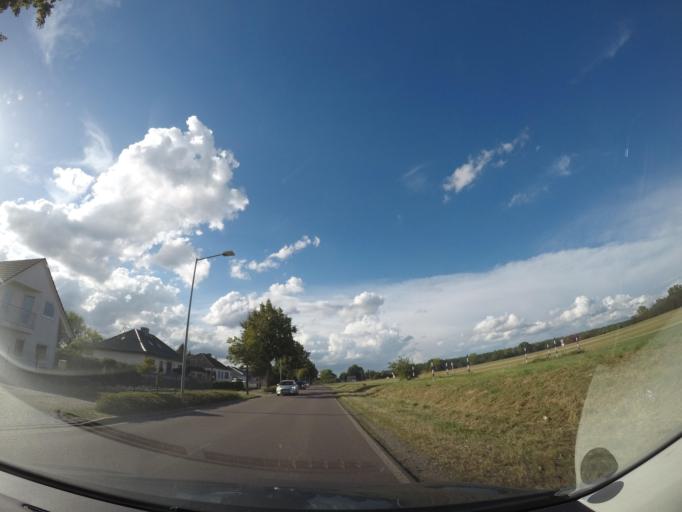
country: DE
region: Saxony-Anhalt
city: Haldensleben I
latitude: 52.2989
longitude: 11.4119
